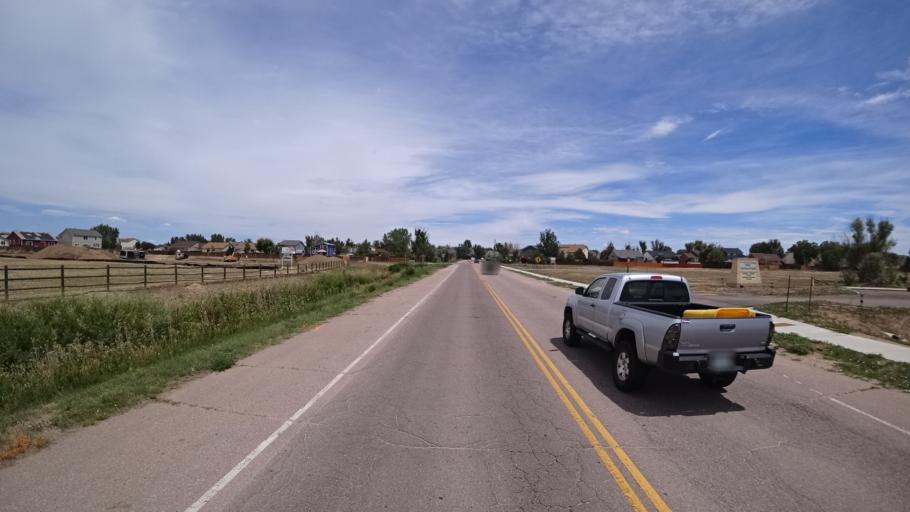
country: US
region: Colorado
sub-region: El Paso County
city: Fountain
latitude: 38.6661
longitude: -104.6820
